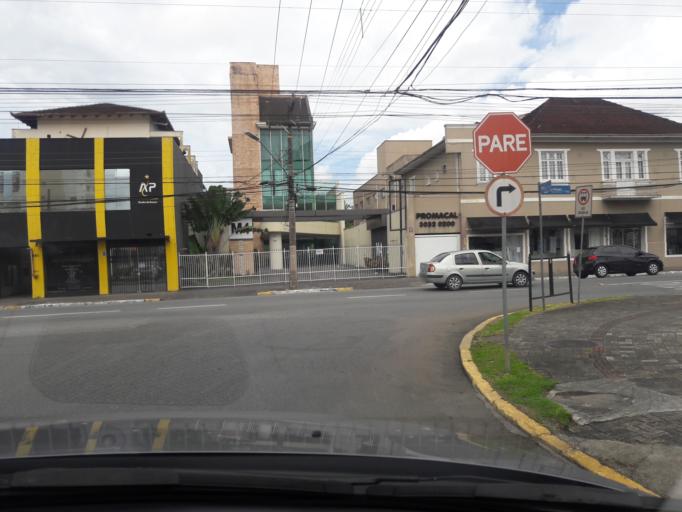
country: BR
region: Santa Catarina
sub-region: Joinville
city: Joinville
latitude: -26.3134
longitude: -48.8456
